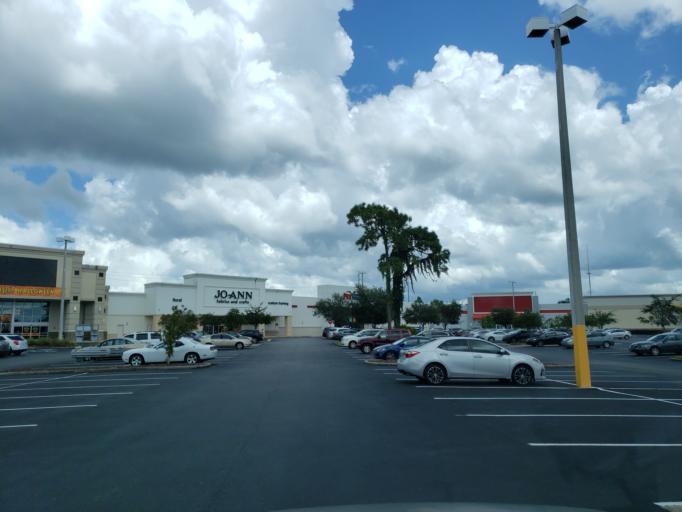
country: US
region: Florida
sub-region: Hillsborough County
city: Pebble Creek
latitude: 28.1169
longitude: -82.3760
